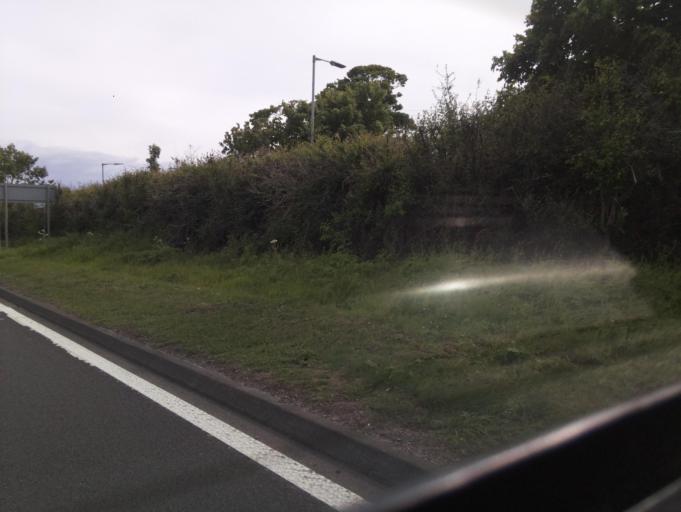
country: GB
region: Scotland
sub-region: The Scottish Borders
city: Eyemouth
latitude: 55.8406
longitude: -2.0760
